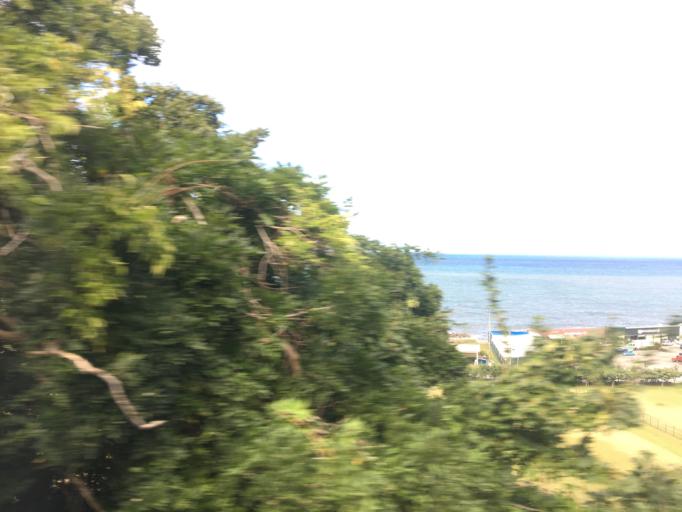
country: JP
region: Aomori
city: Shimokizukuri
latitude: 40.7731
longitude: 140.1844
